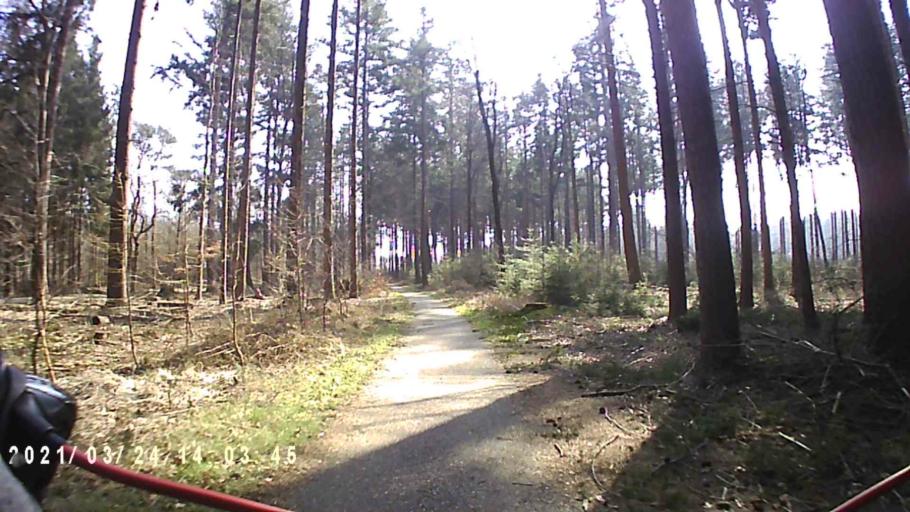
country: NL
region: Friesland
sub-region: Gemeente Smallingerland
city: Drachtstercompagnie
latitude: 53.0793
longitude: 6.2399
